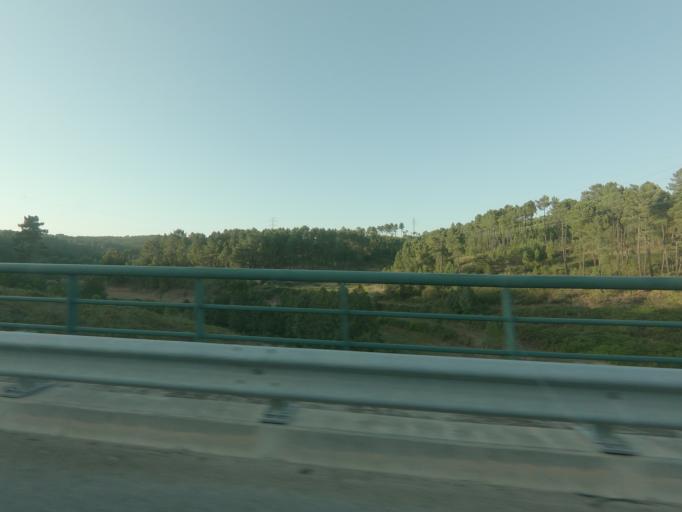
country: PT
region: Vila Real
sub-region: Sabrosa
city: Vilela
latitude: 41.2637
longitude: -7.6709
